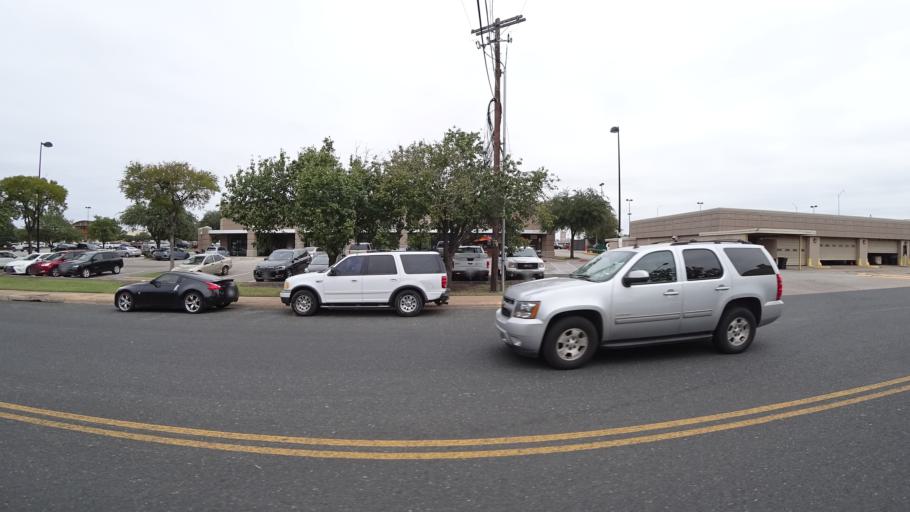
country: US
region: Texas
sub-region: Travis County
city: Austin
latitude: 30.2982
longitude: -97.7192
